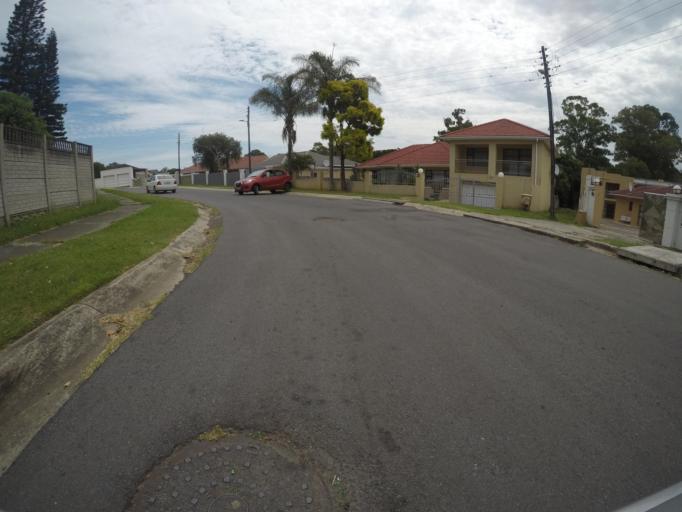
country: ZA
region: Eastern Cape
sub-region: Buffalo City Metropolitan Municipality
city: East London
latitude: -32.9920
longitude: 27.8776
